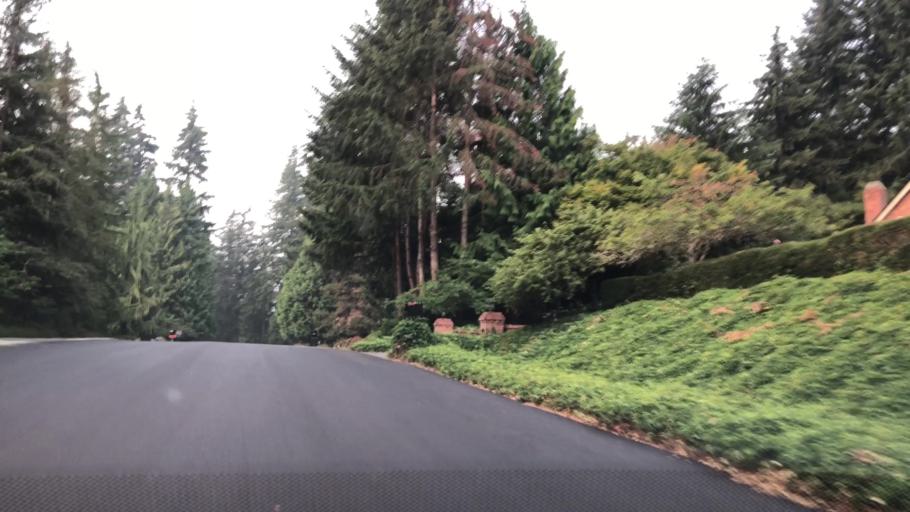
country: US
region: Washington
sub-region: King County
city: Cottage Lake
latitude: 47.7300
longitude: -122.1004
